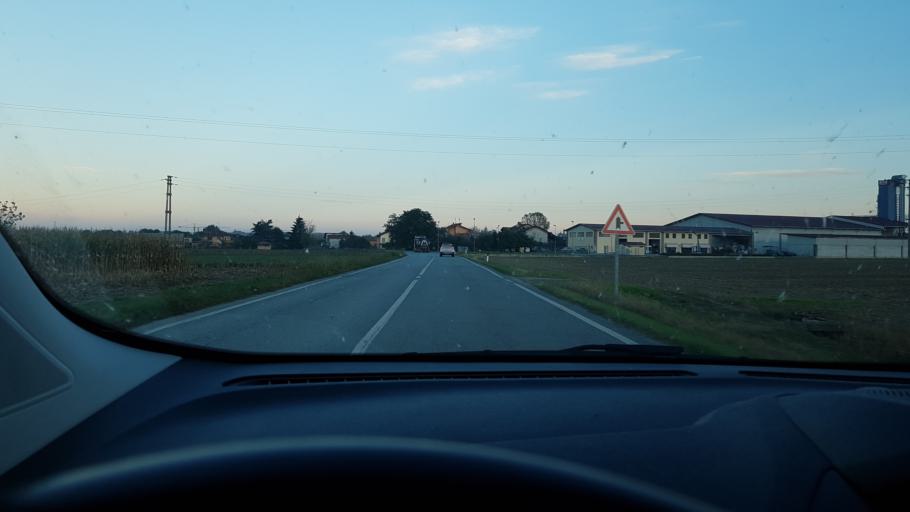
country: IT
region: Piedmont
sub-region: Provincia di Cuneo
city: Fossano
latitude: 44.5543
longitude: 7.6993
